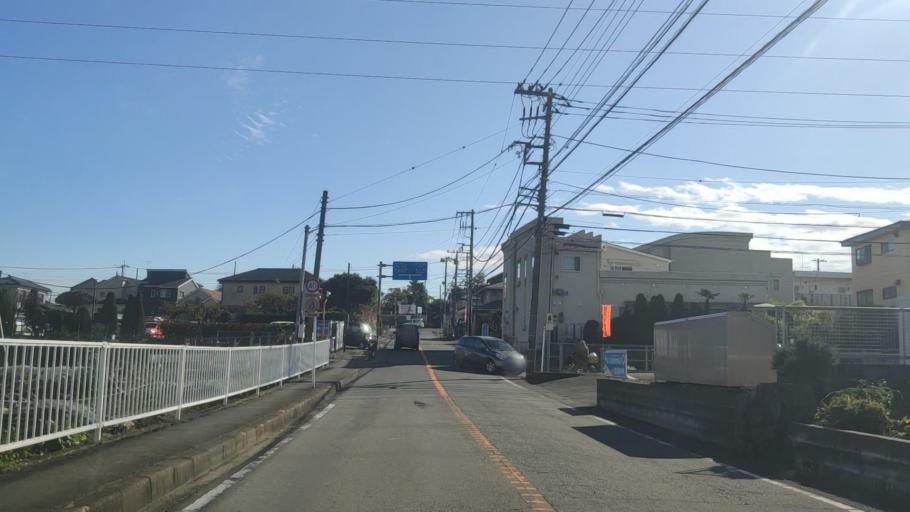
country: JP
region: Kanagawa
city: Atsugi
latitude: 35.4390
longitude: 139.3407
